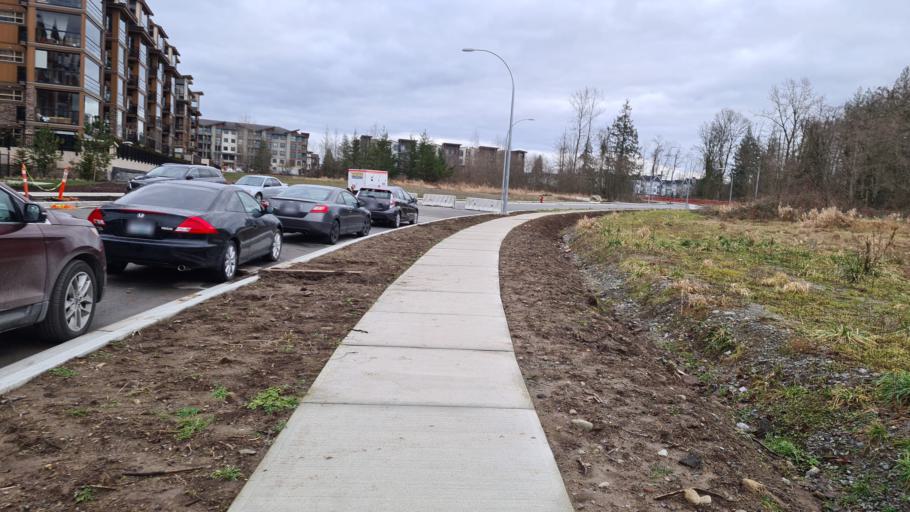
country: CA
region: British Columbia
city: Walnut Grove
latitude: 49.1444
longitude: -122.6492
